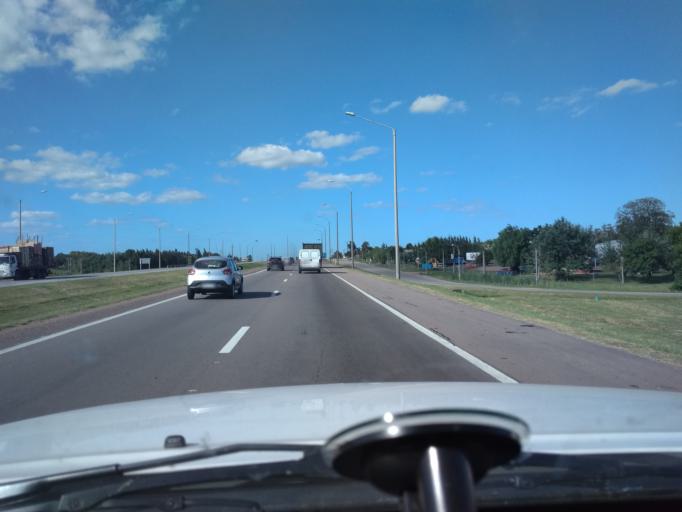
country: UY
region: Canelones
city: La Paz
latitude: -34.7712
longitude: -56.2685
